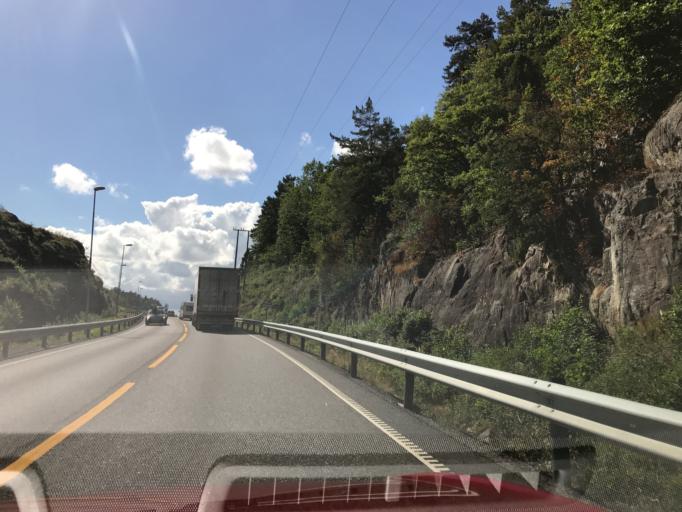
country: NO
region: Telemark
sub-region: Bamble
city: Herre
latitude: 58.9739
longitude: 9.5198
